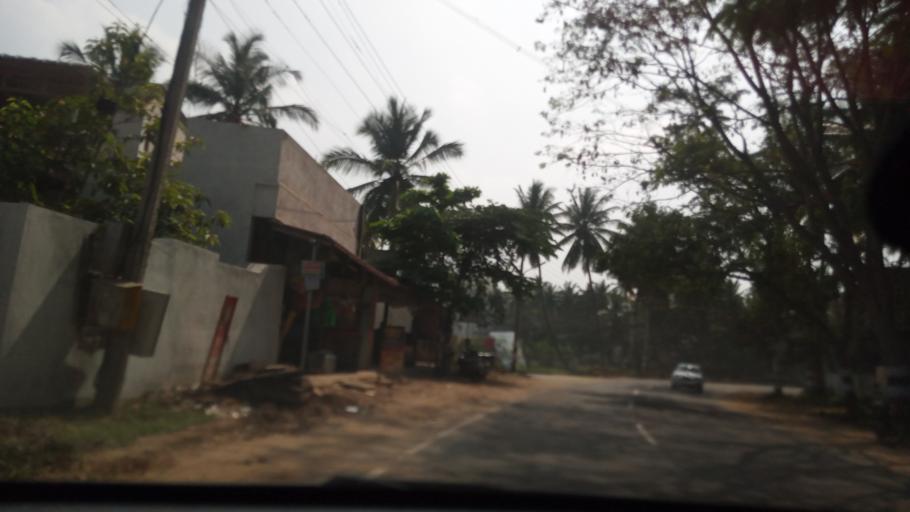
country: IN
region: Tamil Nadu
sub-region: Coimbatore
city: Perur
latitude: 11.0182
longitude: 76.8817
